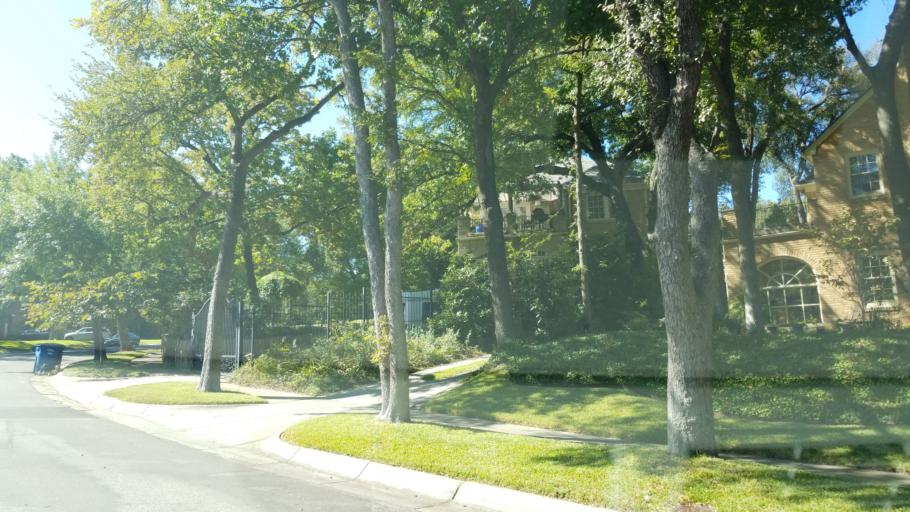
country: US
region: Texas
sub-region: Dallas County
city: Highland Park
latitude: 32.8115
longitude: -96.7495
